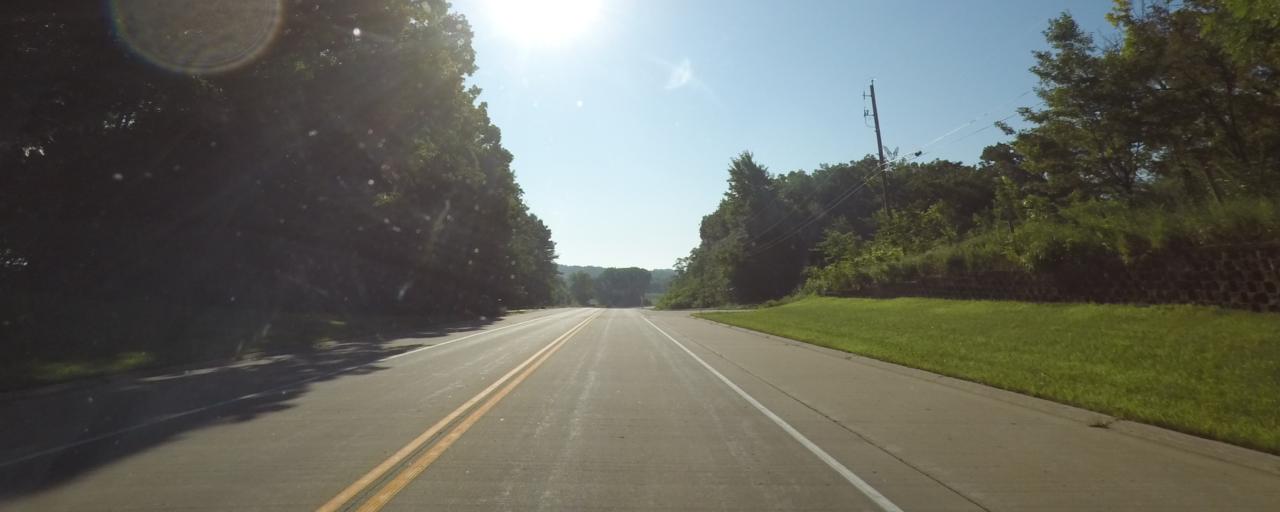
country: US
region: Wisconsin
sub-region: Jefferson County
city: Lake Koshkonong
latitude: 42.9733
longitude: -88.9299
